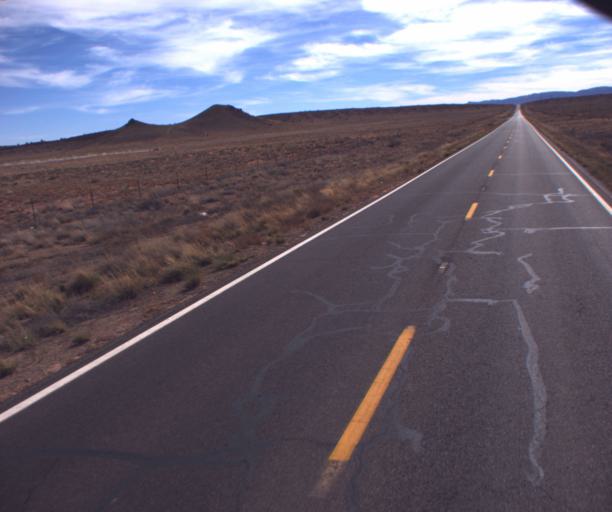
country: US
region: Arizona
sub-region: Navajo County
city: Kayenta
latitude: 36.7732
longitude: -110.2287
